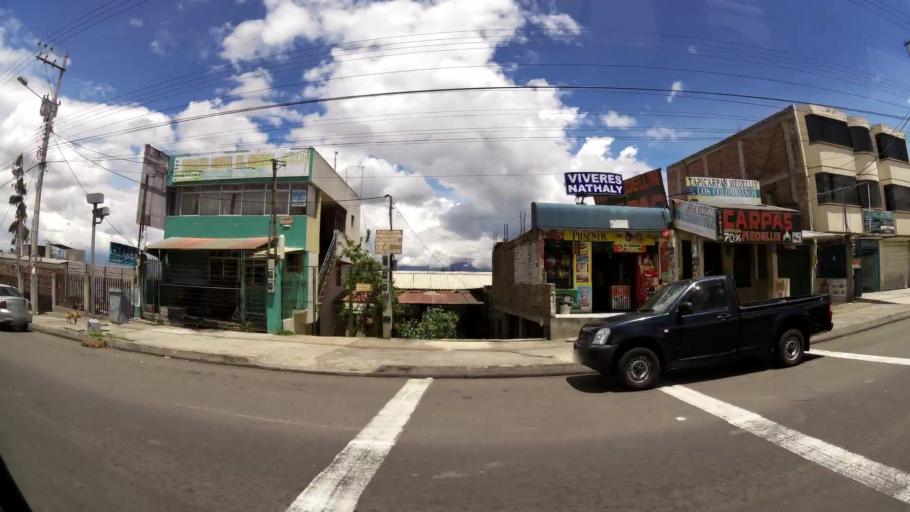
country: EC
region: Tungurahua
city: Ambato
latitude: -1.2764
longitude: -78.6104
